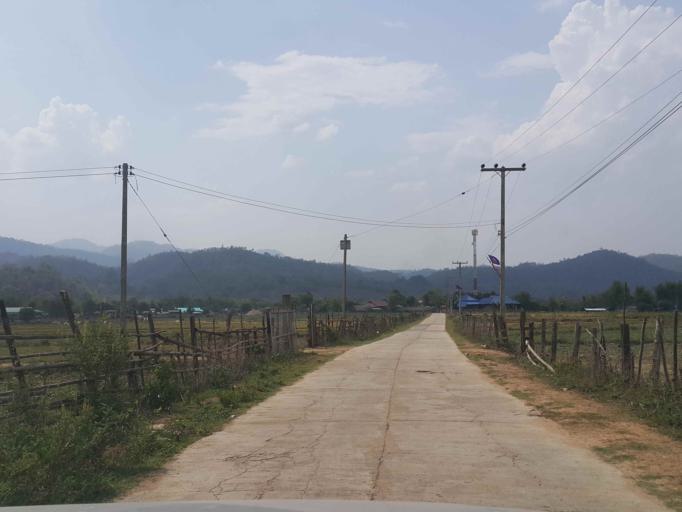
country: TH
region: Chiang Mai
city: Wiang Haeng
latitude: 19.3807
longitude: 98.7190
